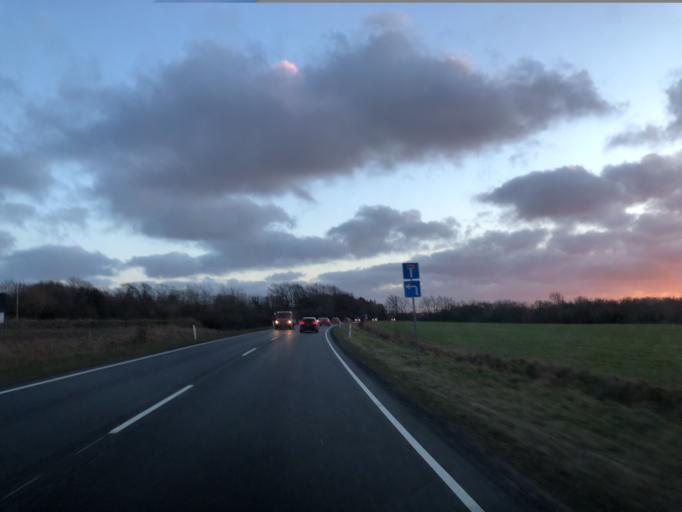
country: DK
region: Central Jutland
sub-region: Herning Kommune
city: Sunds
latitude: 56.1631
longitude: 9.0114
